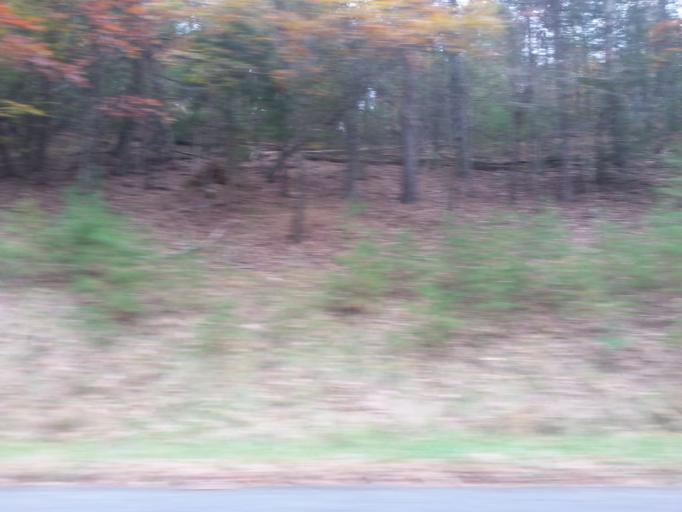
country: US
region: Virginia
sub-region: Bland County
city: Bland
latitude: 37.0615
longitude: -81.0114
